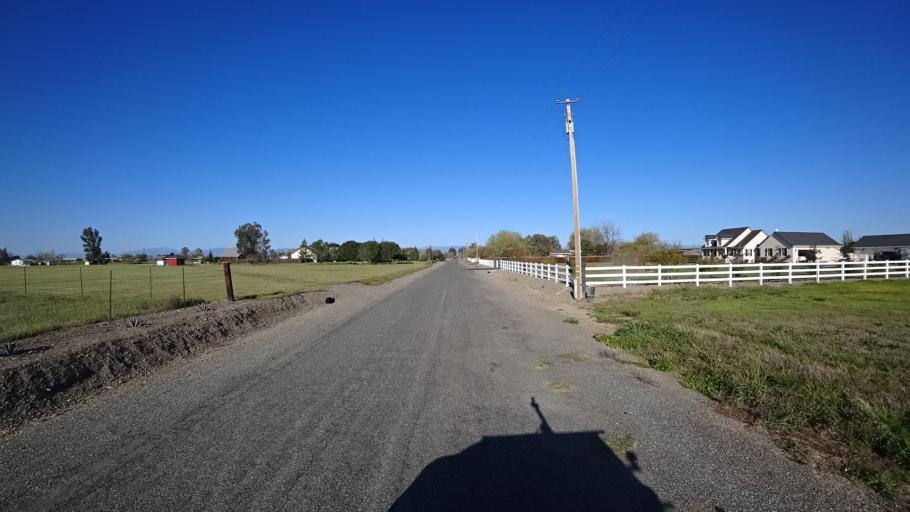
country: US
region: California
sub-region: Glenn County
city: Orland
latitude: 39.7588
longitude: -122.2319
